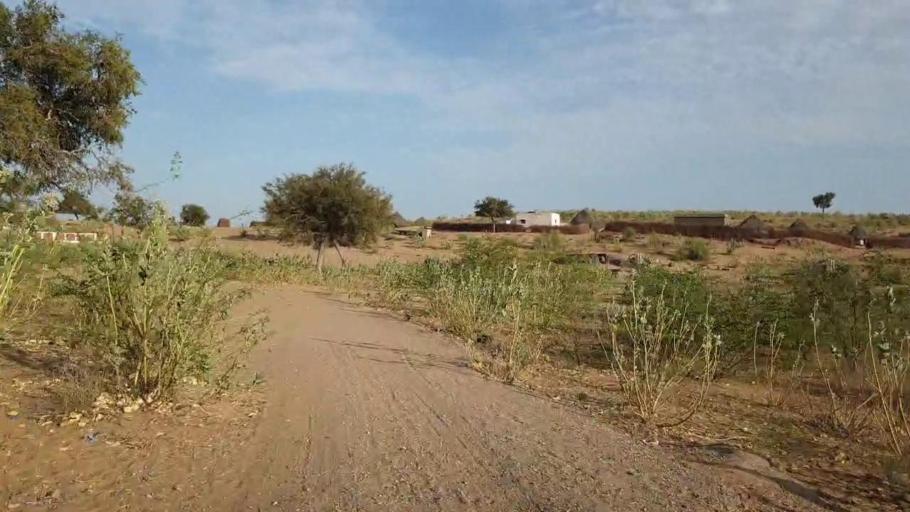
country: PK
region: Sindh
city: Nabisar
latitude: 25.0802
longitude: 69.9899
